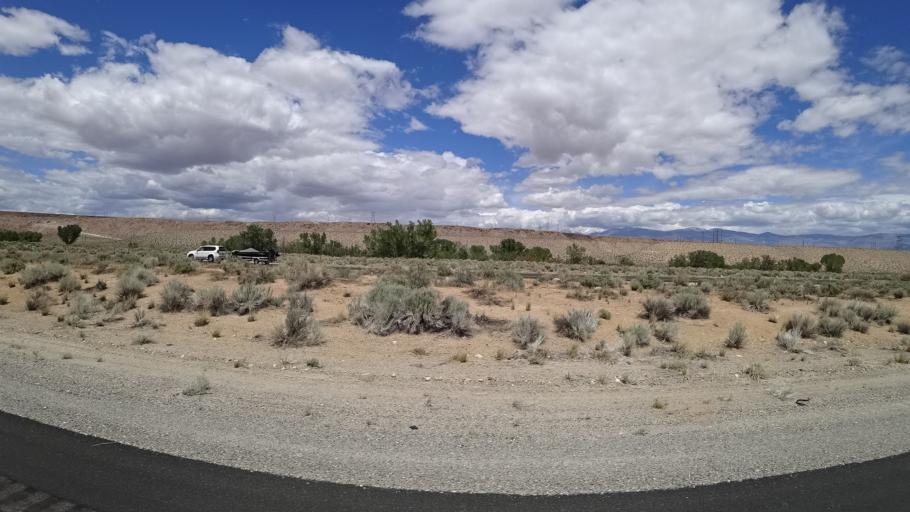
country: US
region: California
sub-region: Inyo County
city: West Bishop
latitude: 37.3987
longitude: -118.5248
